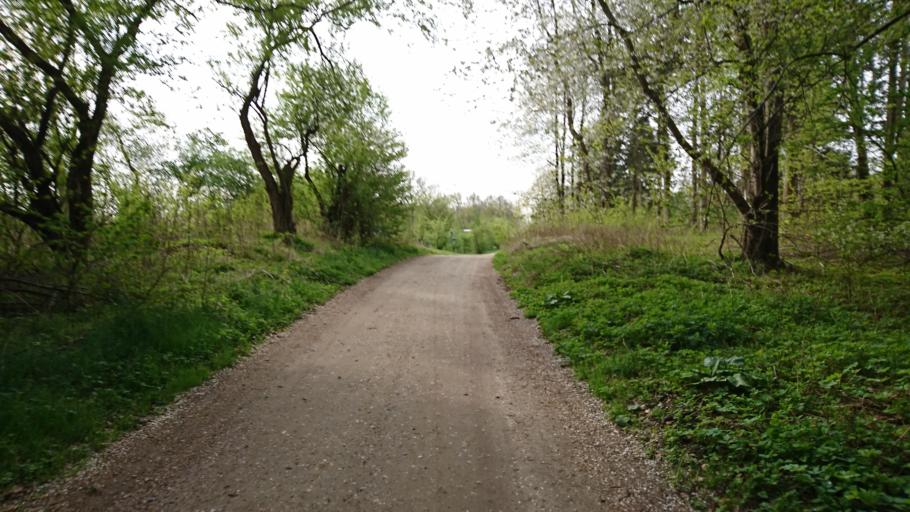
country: DK
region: Capital Region
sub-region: Ballerup Kommune
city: Ballerup
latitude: 55.7434
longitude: 12.3998
